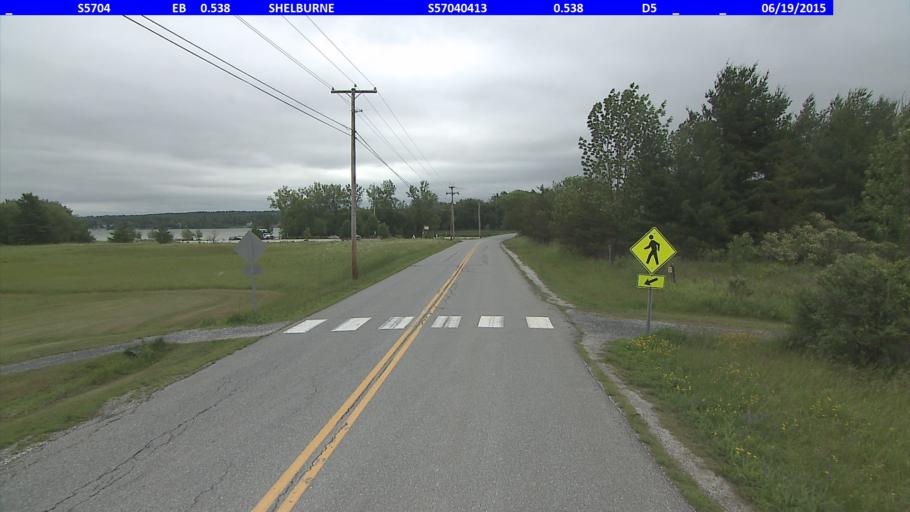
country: US
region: Vermont
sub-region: Chittenden County
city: Burlington
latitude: 44.3982
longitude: -73.2370
